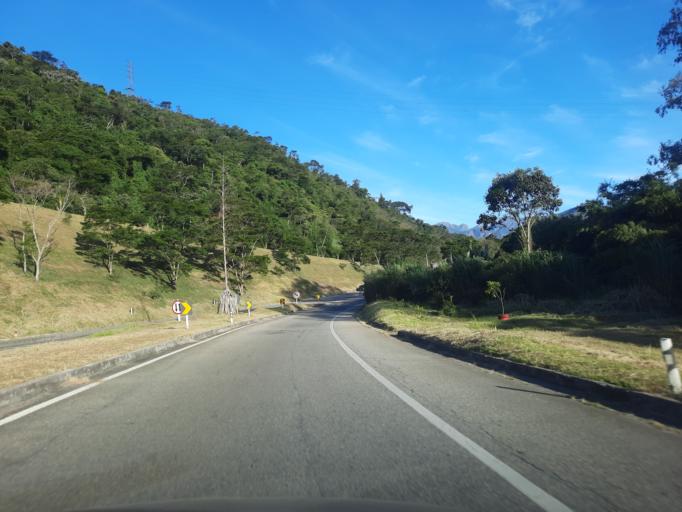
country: BR
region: Rio de Janeiro
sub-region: Petropolis
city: Petropolis
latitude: -22.4082
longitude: -43.1470
